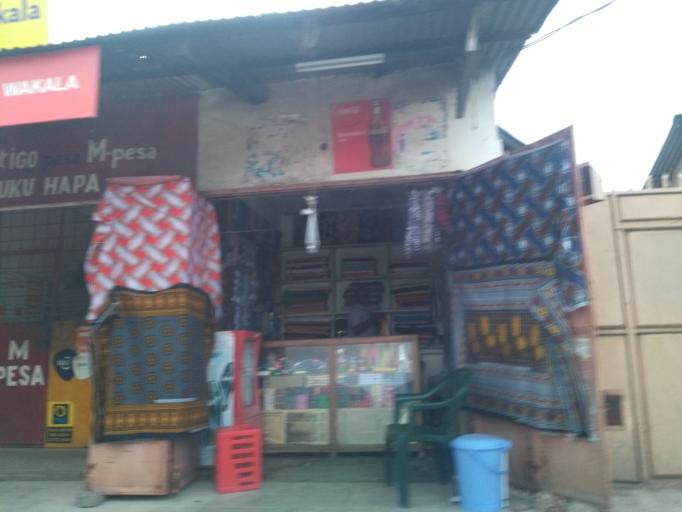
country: TZ
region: Dar es Salaam
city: Magomeni
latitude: -6.7966
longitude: 39.2665
